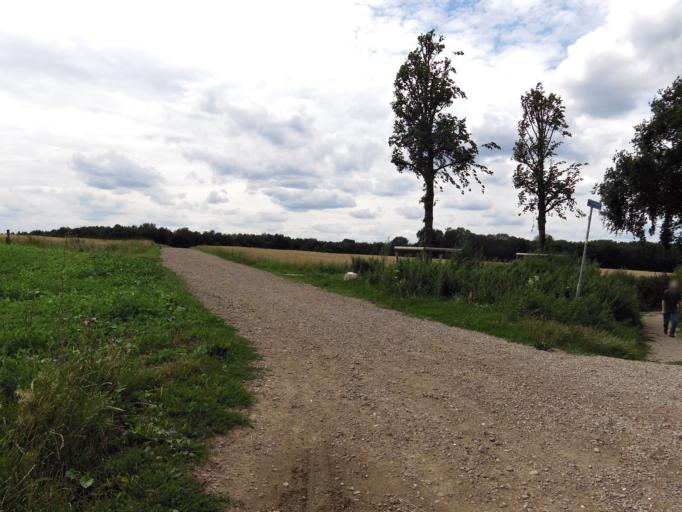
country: NL
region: Limburg
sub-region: Gemeente Schinnen
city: Doenrade
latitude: 50.9823
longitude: 5.8908
